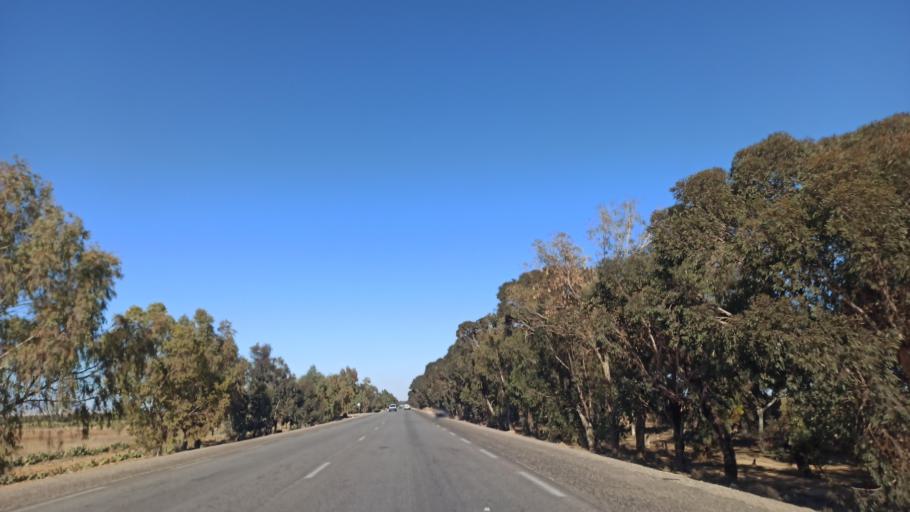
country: TN
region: Sidi Bu Zayd
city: Jilma
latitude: 35.1844
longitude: 9.3740
